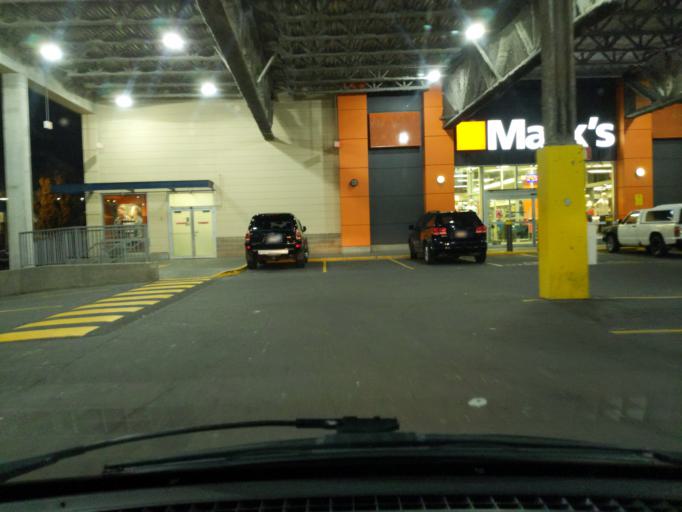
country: CA
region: British Columbia
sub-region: Fraser Valley Regional District
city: North Vancouver
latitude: 49.2592
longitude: -123.0319
